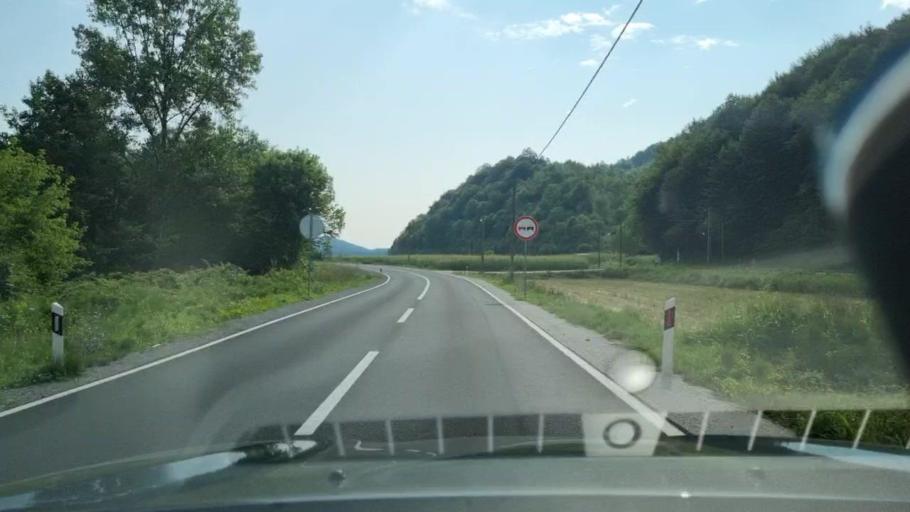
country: BA
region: Federation of Bosnia and Herzegovina
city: Otoka
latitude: 44.9812
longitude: 16.2052
